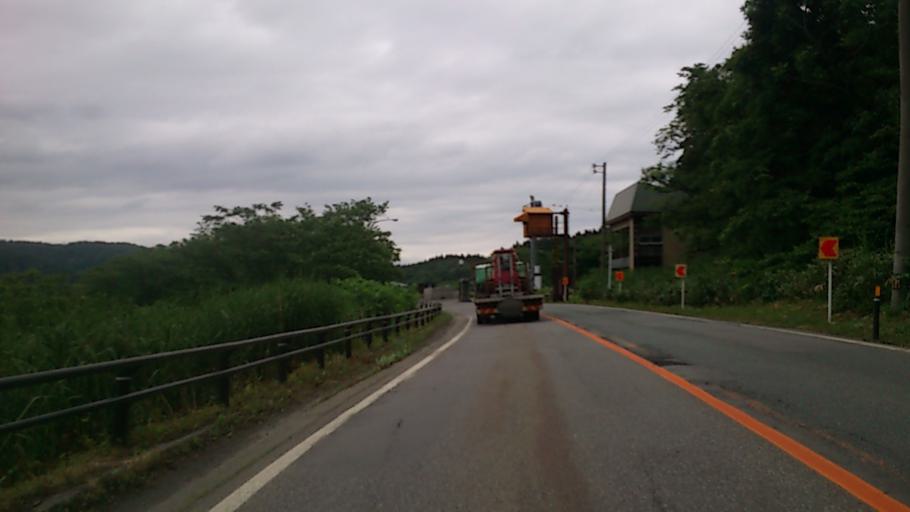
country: JP
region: Yamagata
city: Shinjo
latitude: 38.7216
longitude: 140.1971
